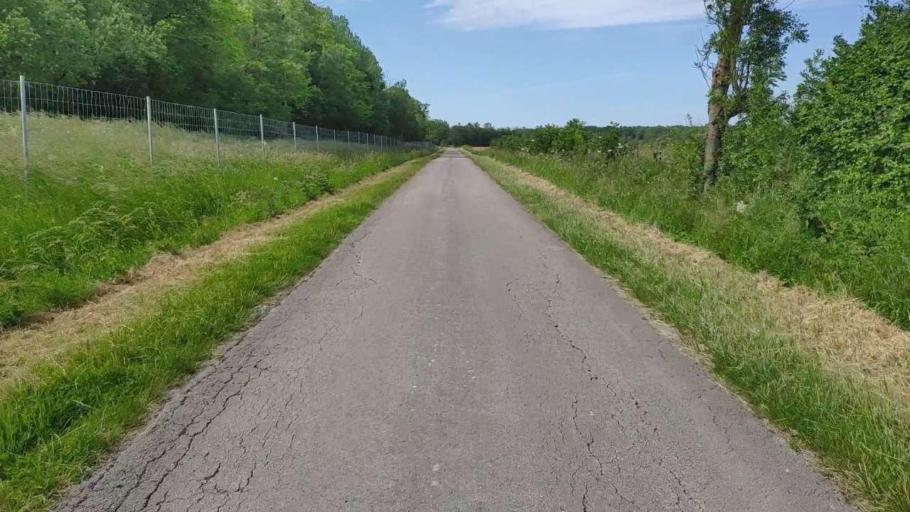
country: FR
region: Franche-Comte
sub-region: Departement du Jura
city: Bletterans
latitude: 46.6840
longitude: 5.4274
